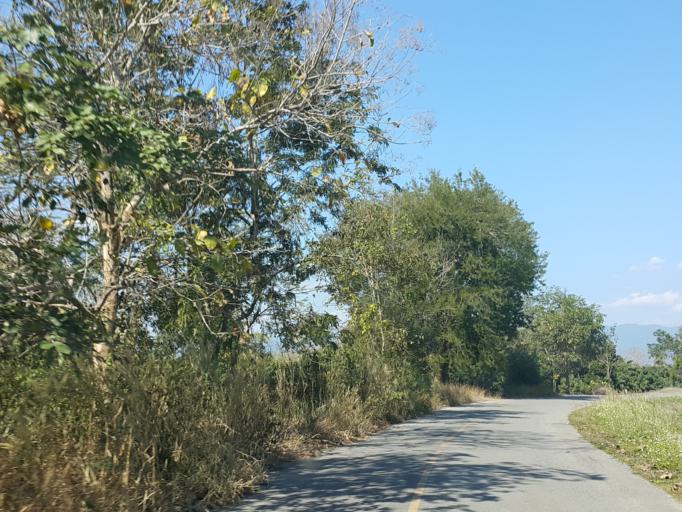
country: TH
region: Chiang Mai
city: Mae Taeng
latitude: 19.0871
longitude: 98.9505
